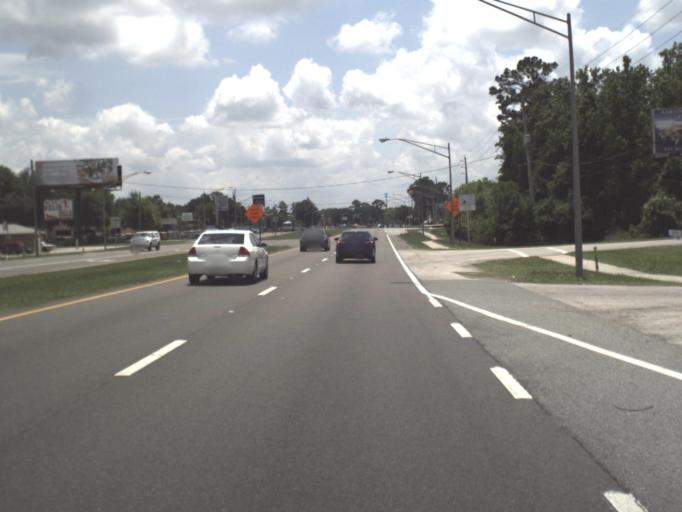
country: US
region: Florida
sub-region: Clay County
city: Bellair-Meadowbrook Terrace
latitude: 30.2187
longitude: -81.7370
